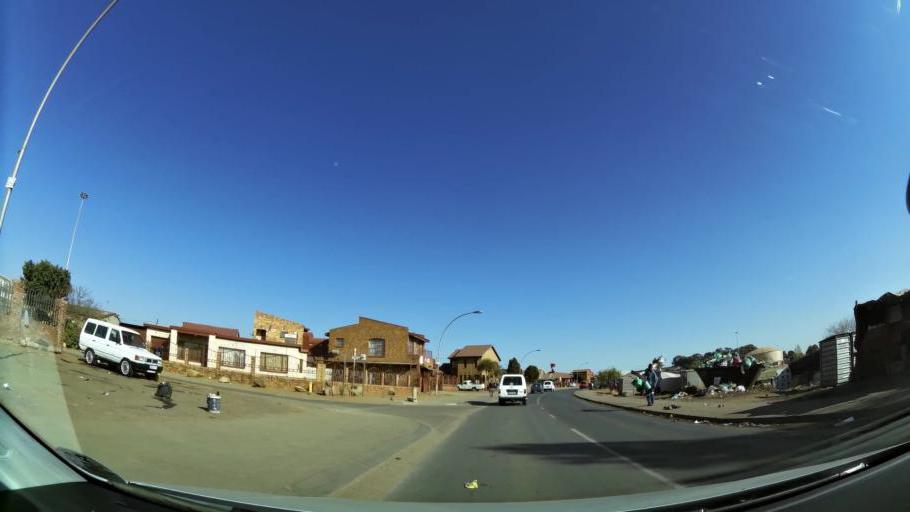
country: ZA
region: Gauteng
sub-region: Ekurhuleni Metropolitan Municipality
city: Tembisa
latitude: -26.0183
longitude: 28.2306
